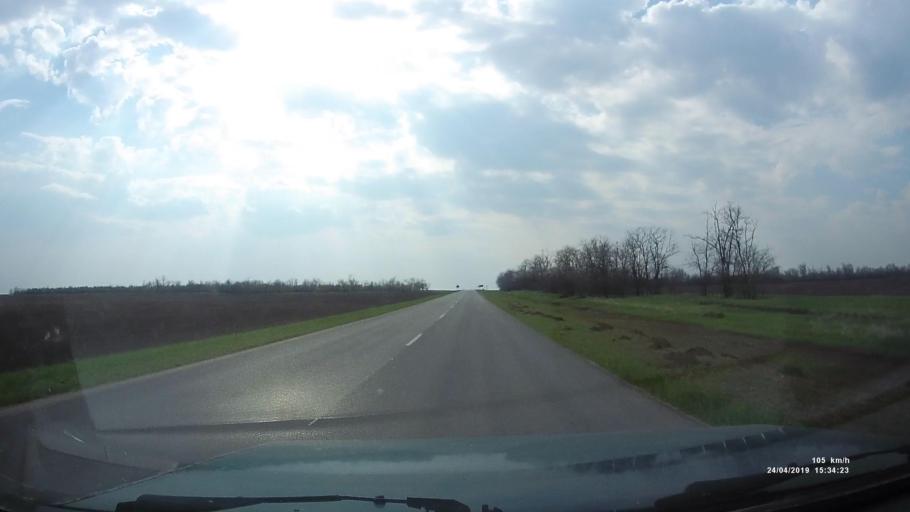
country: RU
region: Kalmykiya
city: Yashalta
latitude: 46.5992
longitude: 42.9172
